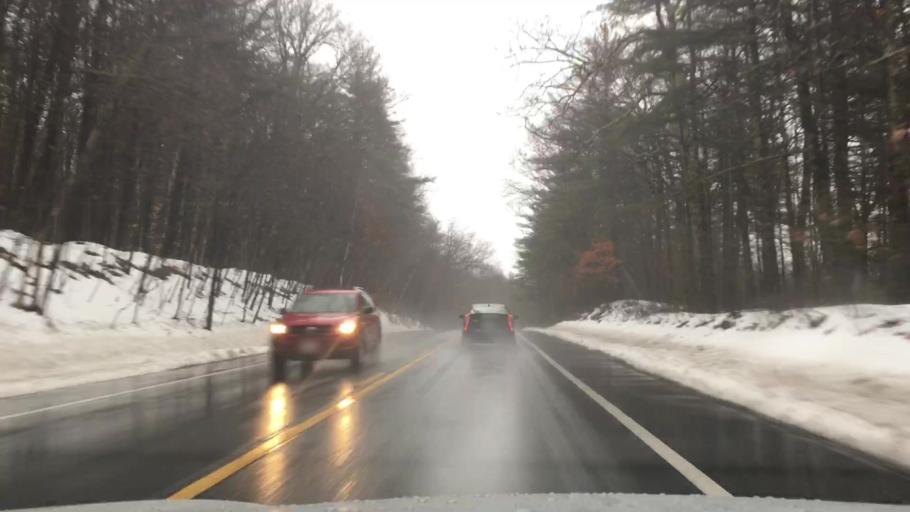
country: US
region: Massachusetts
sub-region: Franklin County
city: Shutesbury
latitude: 42.4320
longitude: -72.3964
